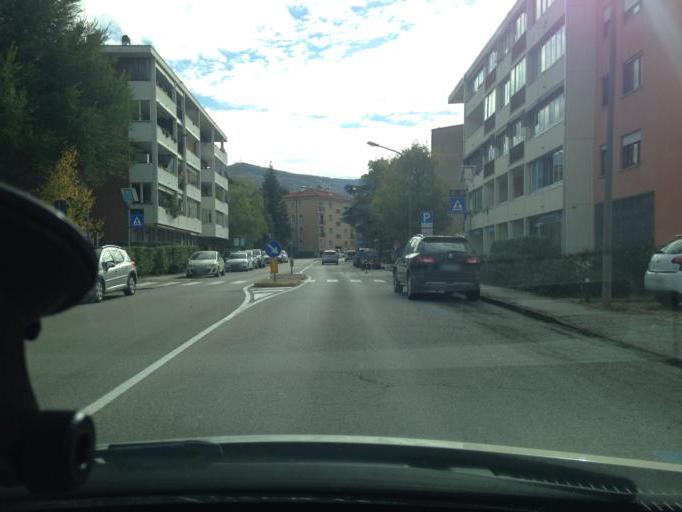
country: IT
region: Trentino-Alto Adige
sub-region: Provincia di Trento
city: Rovereto
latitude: 45.8954
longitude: 11.0373
